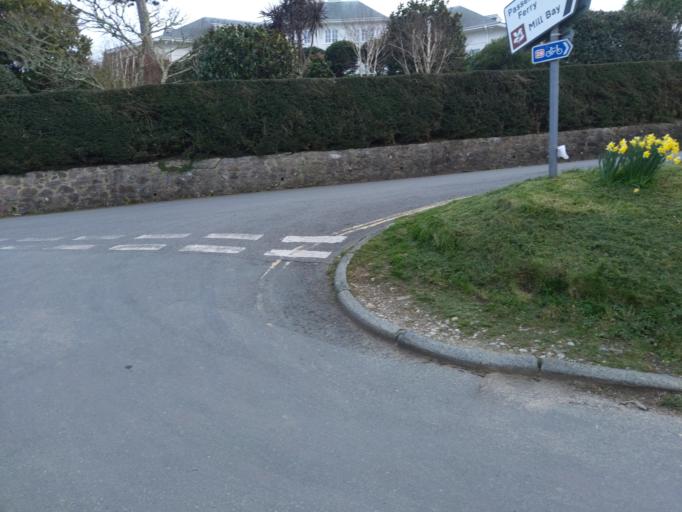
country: GB
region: England
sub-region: Devon
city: Salcombe
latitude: 50.2371
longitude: -3.7551
